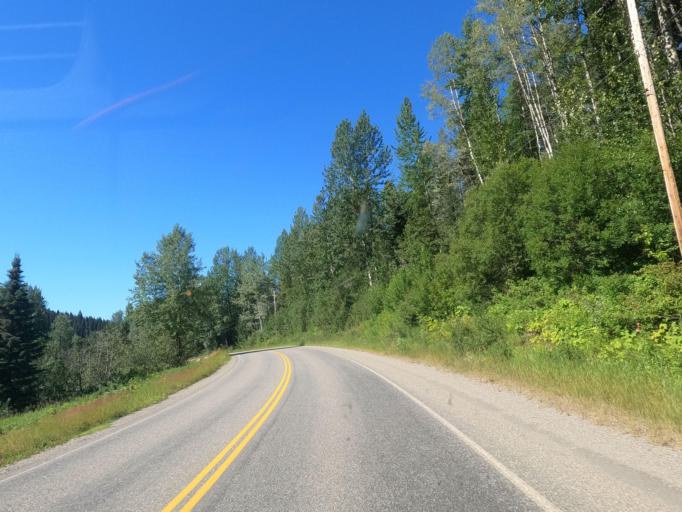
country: CA
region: British Columbia
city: Quesnel
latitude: 53.0433
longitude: -121.9720
